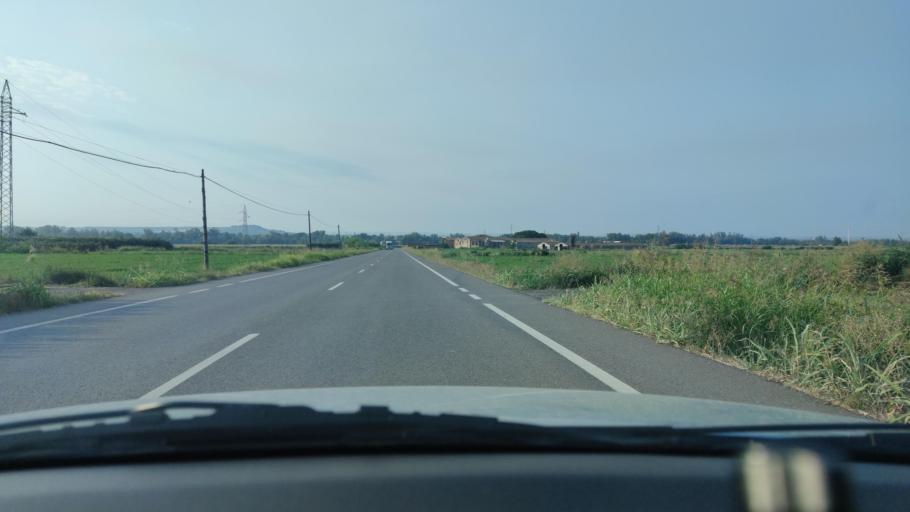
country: ES
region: Catalonia
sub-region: Provincia de Lleida
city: Torres de Segre
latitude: 41.5486
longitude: 0.5099
